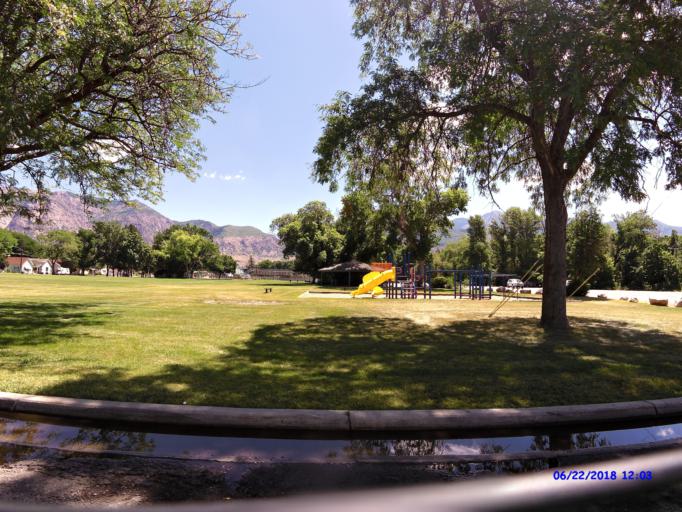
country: US
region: Utah
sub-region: Weber County
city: Ogden
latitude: 41.2368
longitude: -111.9653
